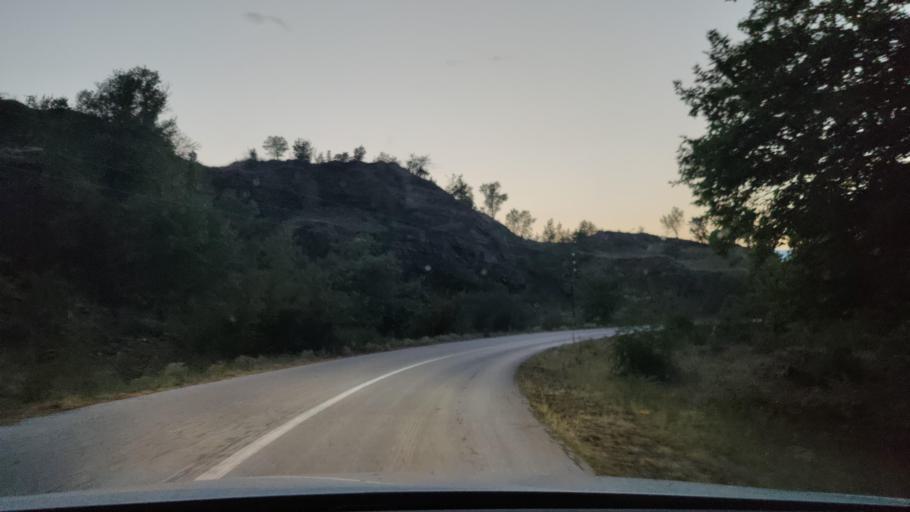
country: GR
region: Central Macedonia
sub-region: Nomos Serron
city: Chrysochorafa
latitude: 41.1971
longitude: 23.0835
